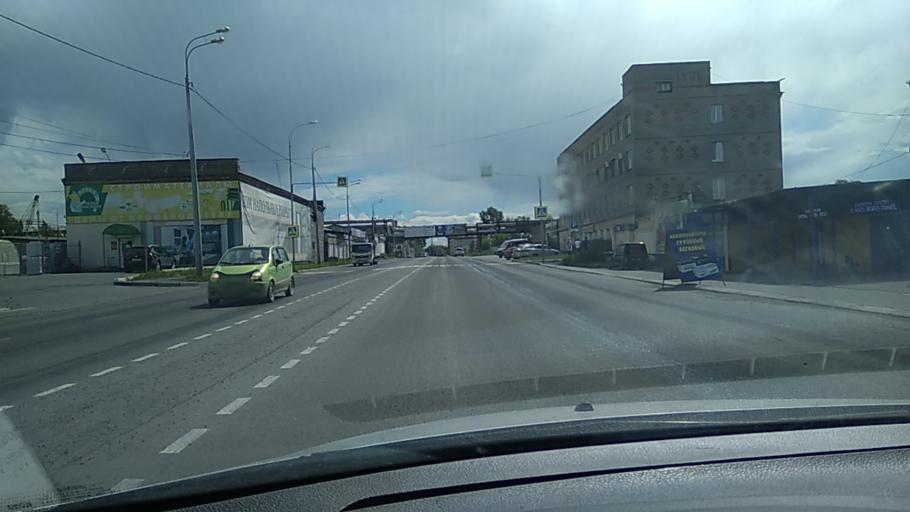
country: RU
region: Sverdlovsk
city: Nizhniy Tagil
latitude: 57.9197
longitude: 59.9889
